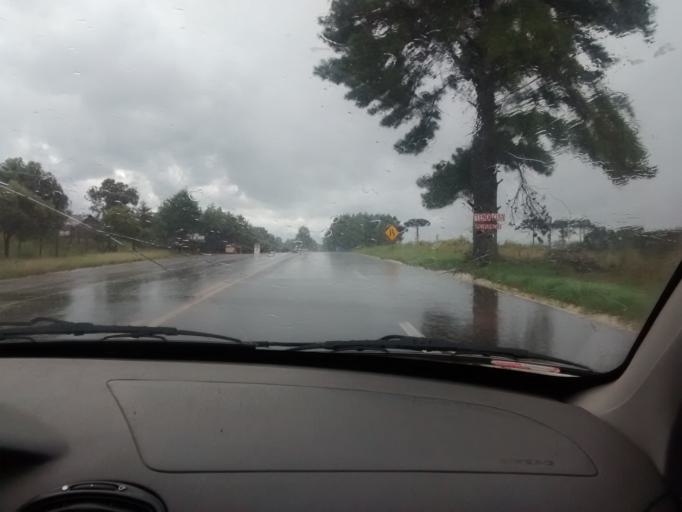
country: BR
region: Rio Grande do Sul
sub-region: Vacaria
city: Vacaria
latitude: -28.5451
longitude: -50.9742
